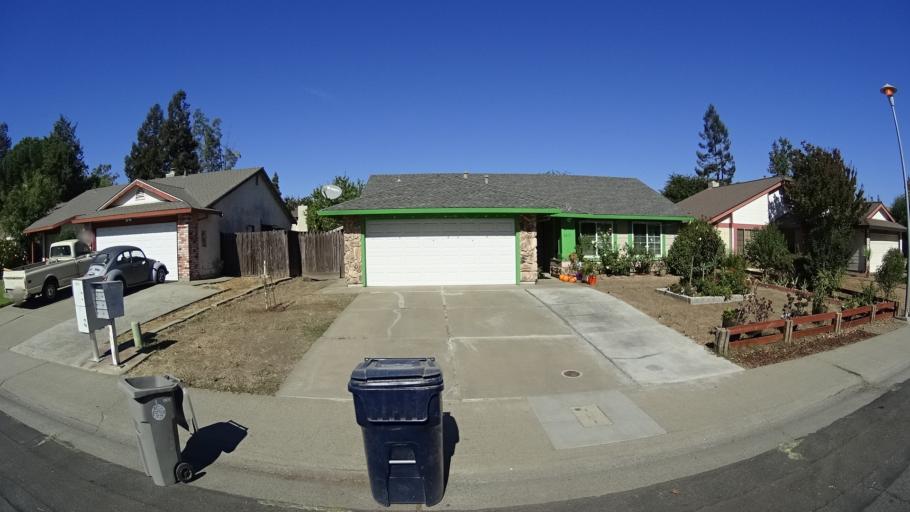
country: US
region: California
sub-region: Sacramento County
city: Parkway
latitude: 38.4652
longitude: -121.4543
